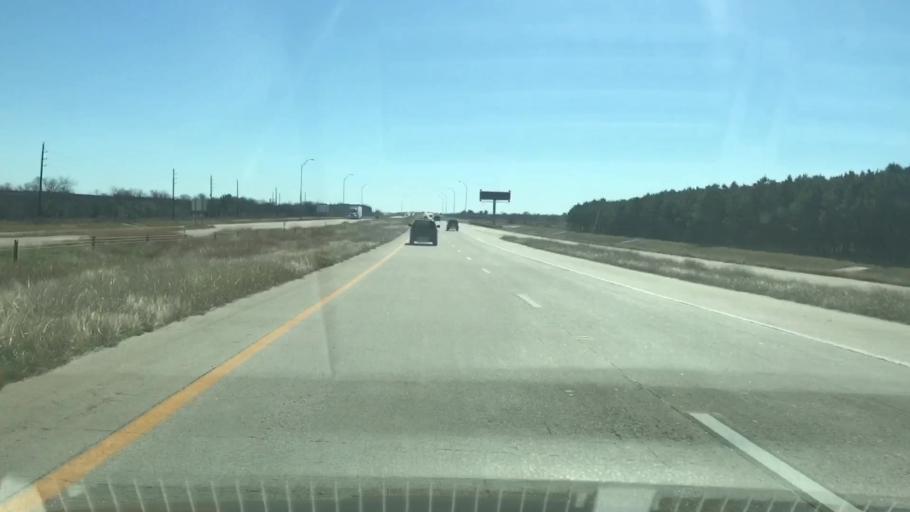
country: US
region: Texas
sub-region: Harris County
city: Cypress
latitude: 29.9016
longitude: -95.7584
